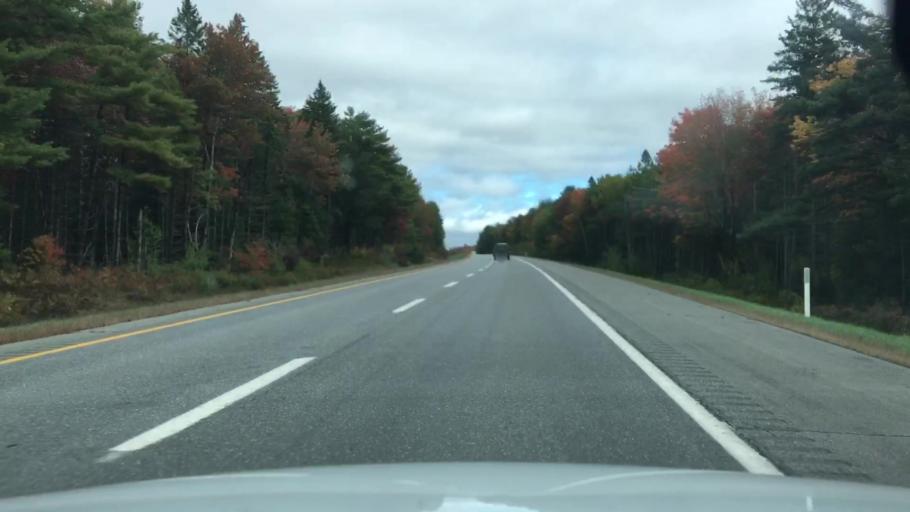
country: US
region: Maine
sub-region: Penobscot County
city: Carmel
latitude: 44.7742
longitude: -69.0353
